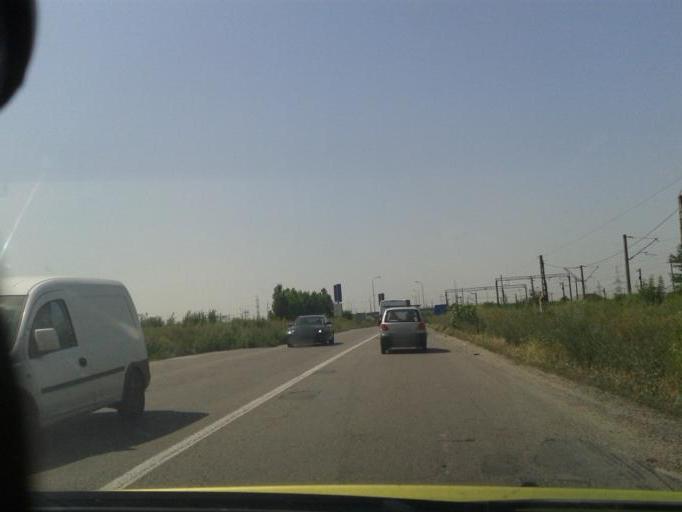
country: RO
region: Ilfov
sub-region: Comuna Glina
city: Catelu
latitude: 44.4121
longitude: 26.2354
